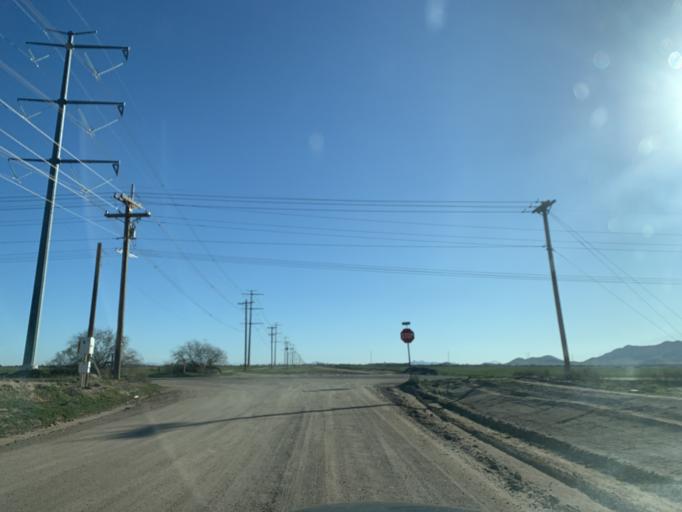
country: US
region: Arizona
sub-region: Pinal County
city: Casa Grande
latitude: 32.8509
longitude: -111.6711
